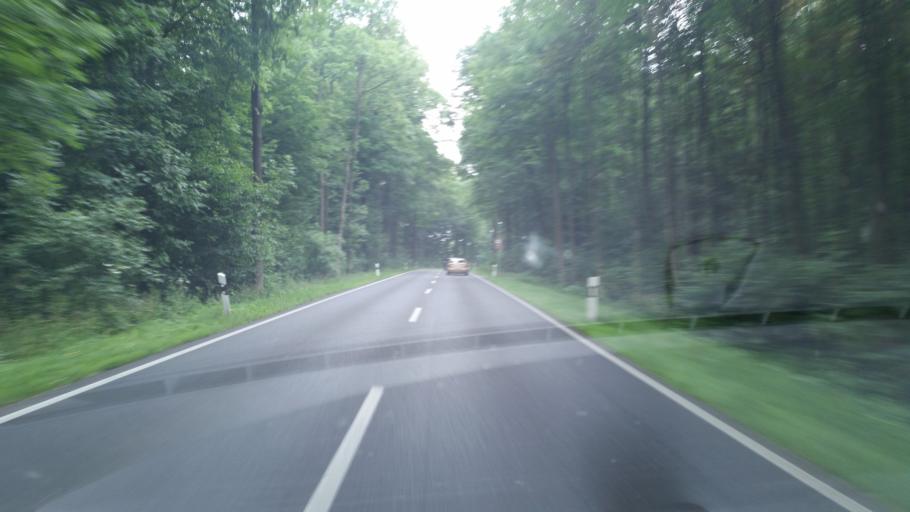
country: DE
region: Saxony
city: Neustadt in Sachsen
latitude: 51.0031
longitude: 14.2366
